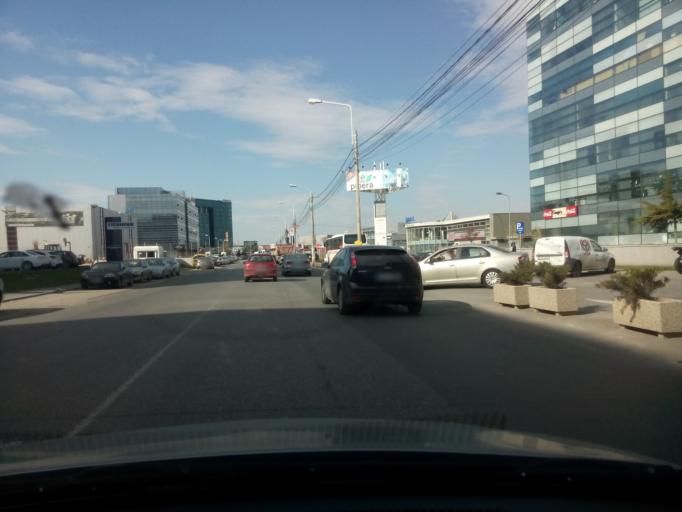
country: RO
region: Ilfov
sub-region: Voluntari City
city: Voluntari
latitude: 44.4891
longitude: 26.1264
